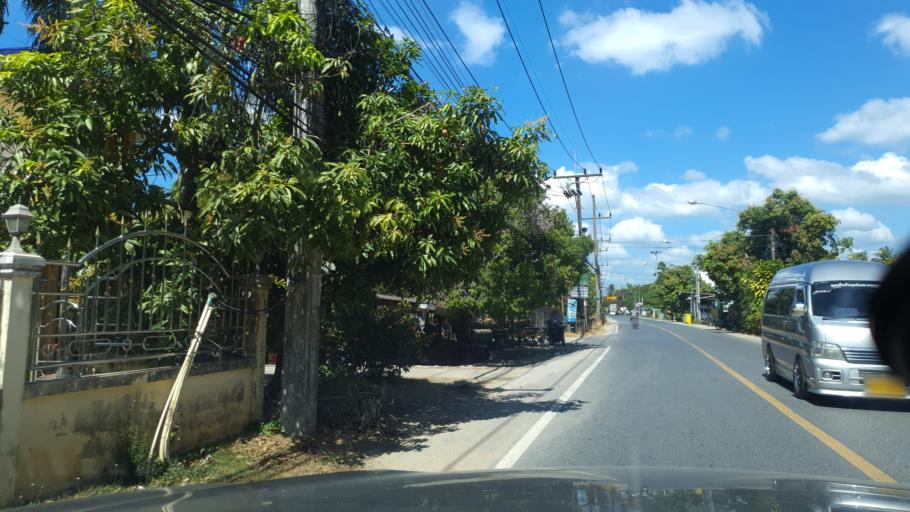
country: TH
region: Phuket
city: Thalang
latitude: 8.1263
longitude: 98.3081
